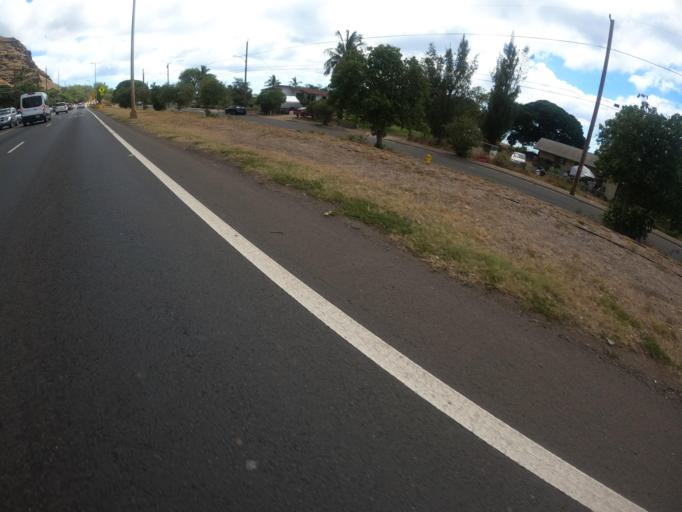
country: US
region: Hawaii
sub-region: Honolulu County
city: Nanakuli
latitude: 21.3713
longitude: -158.1370
